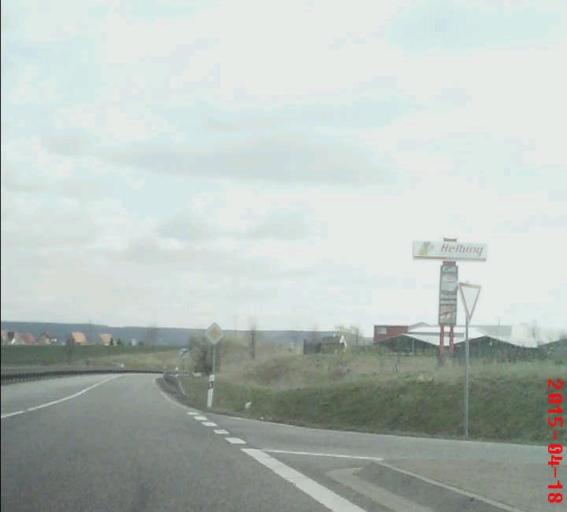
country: DE
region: Thuringia
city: Leinefelde
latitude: 51.3933
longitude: 10.3435
